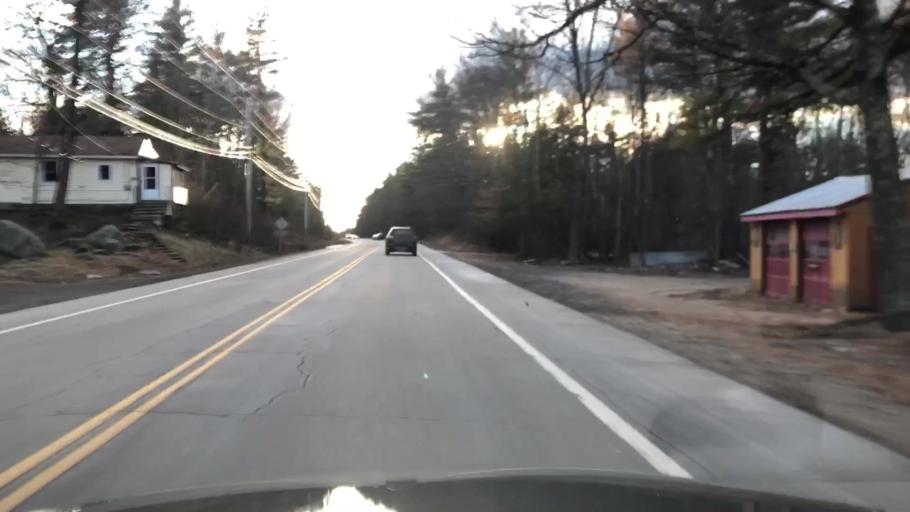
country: US
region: New Hampshire
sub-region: Hillsborough County
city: Brookline
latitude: 42.7821
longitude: -71.6617
